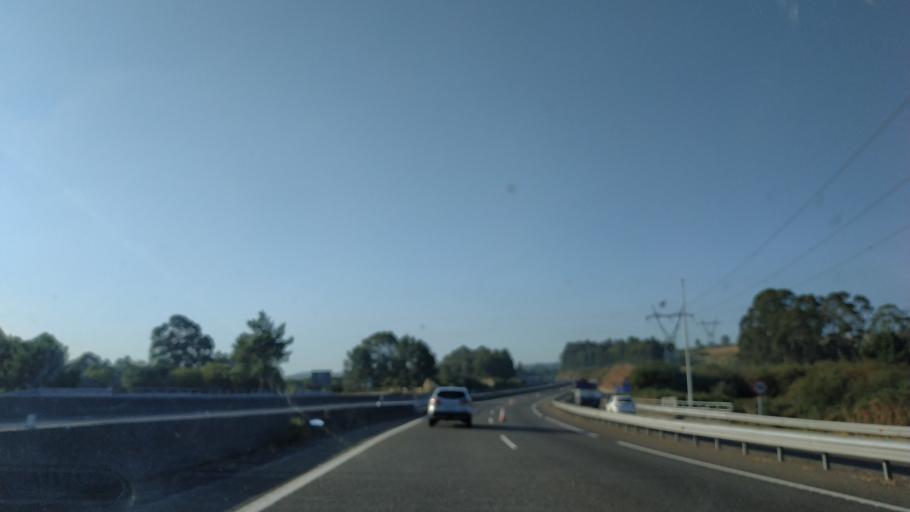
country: ES
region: Galicia
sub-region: Provincia da Coruna
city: Arteixo
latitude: 43.3072
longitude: -8.4746
